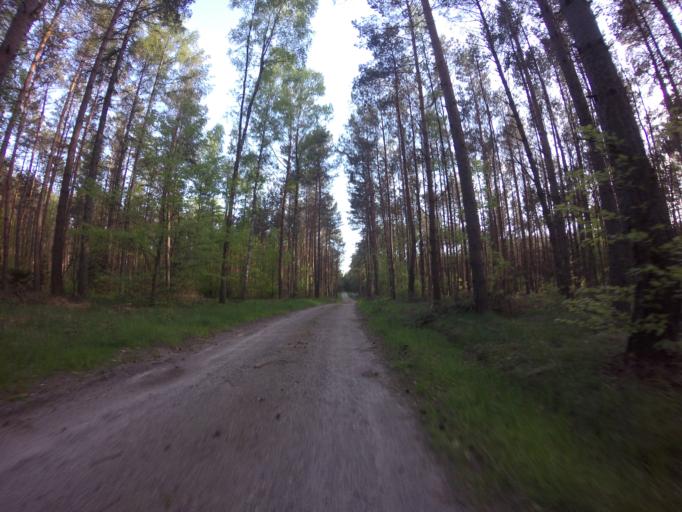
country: PL
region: West Pomeranian Voivodeship
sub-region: Powiat choszczenski
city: Drawno
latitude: 53.2082
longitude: 15.6769
